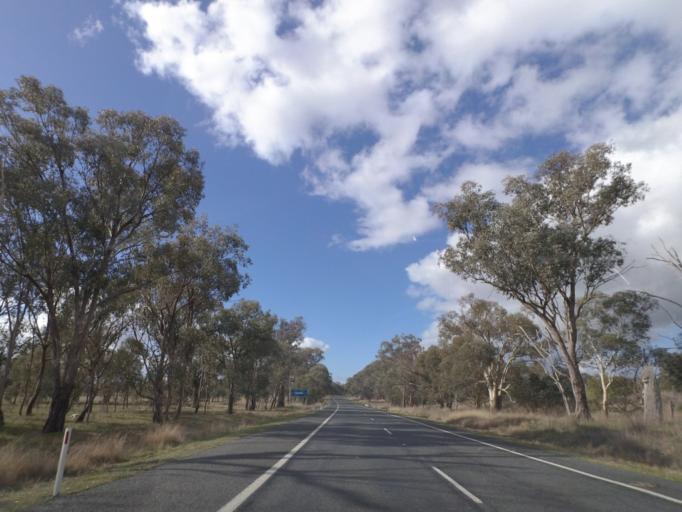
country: AU
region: New South Wales
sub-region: Greater Hume Shire
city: Holbrook
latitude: -35.6763
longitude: 147.3727
